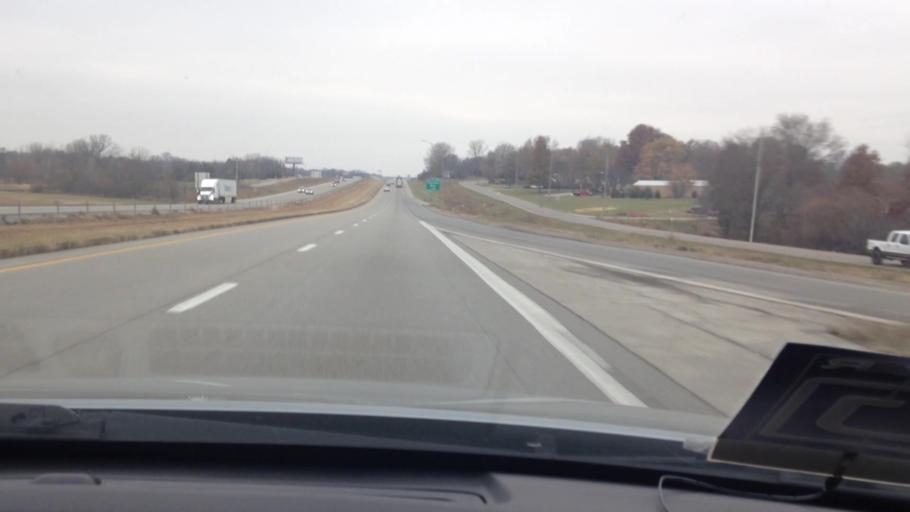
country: US
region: Missouri
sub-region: Cass County
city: Peculiar
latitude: 38.7253
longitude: -94.4569
